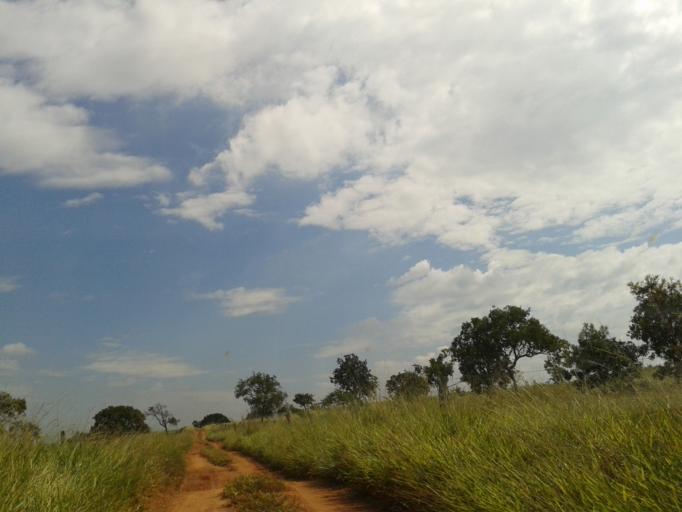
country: BR
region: Minas Gerais
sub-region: Campina Verde
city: Campina Verde
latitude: -19.3927
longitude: -49.6405
